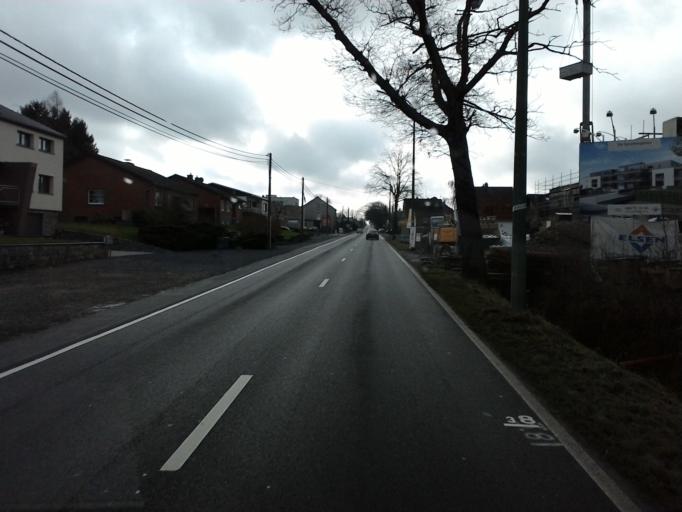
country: BE
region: Wallonia
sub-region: Province de Liege
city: Raeren
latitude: 50.6895
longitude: 6.0806
